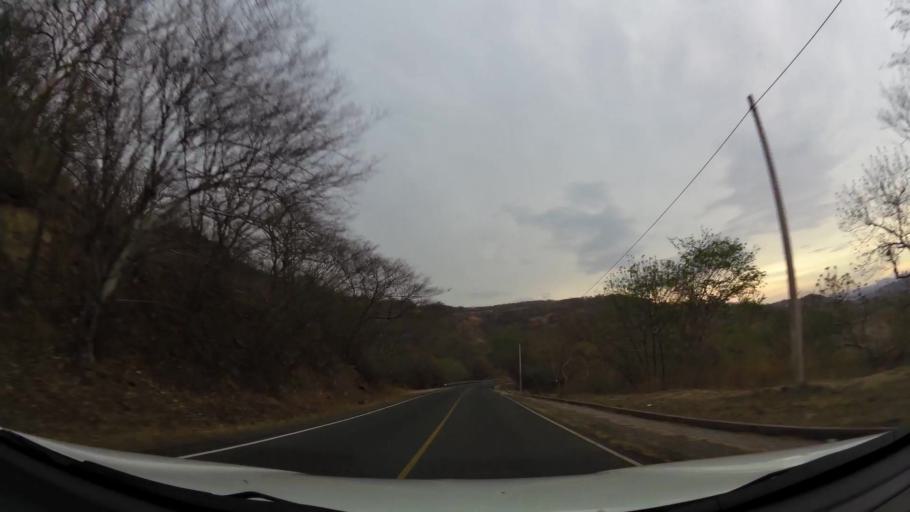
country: NI
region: Leon
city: La Jicaral
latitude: 12.6785
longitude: -86.4270
